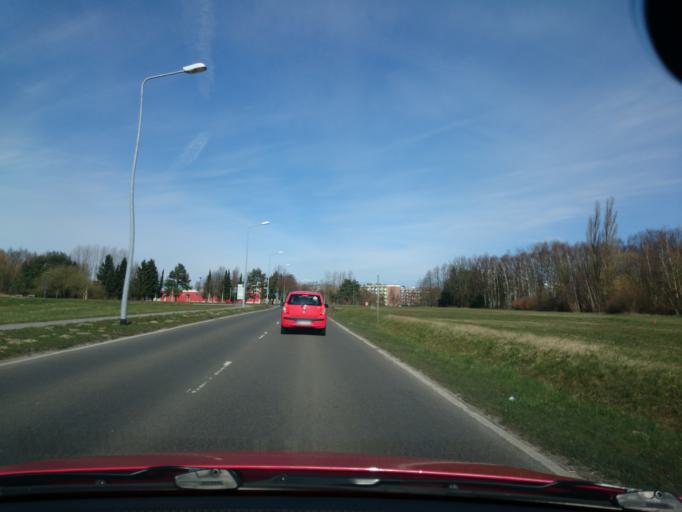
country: DE
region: Mecklenburg-Vorpommern
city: Lambrechtshagen
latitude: 54.1124
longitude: 12.0528
